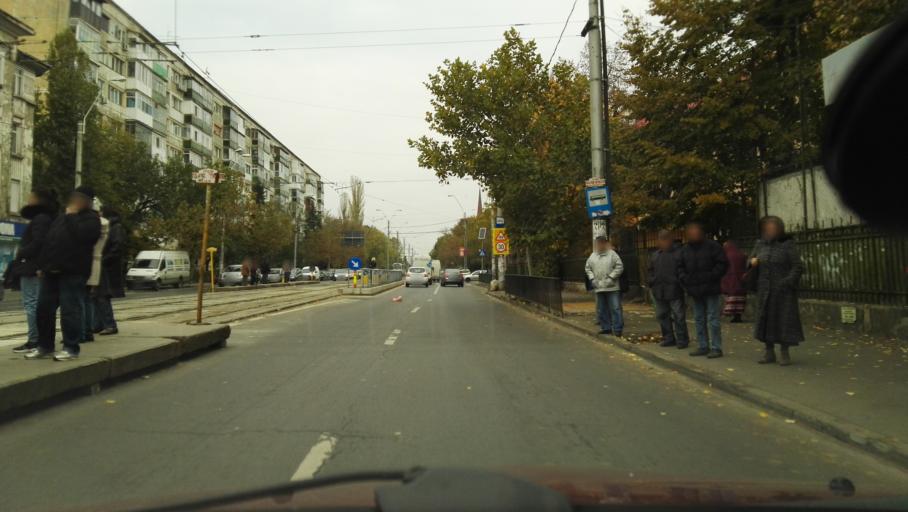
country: RO
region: Bucuresti
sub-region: Municipiul Bucuresti
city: Bucuresti
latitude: 44.4058
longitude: 26.0954
